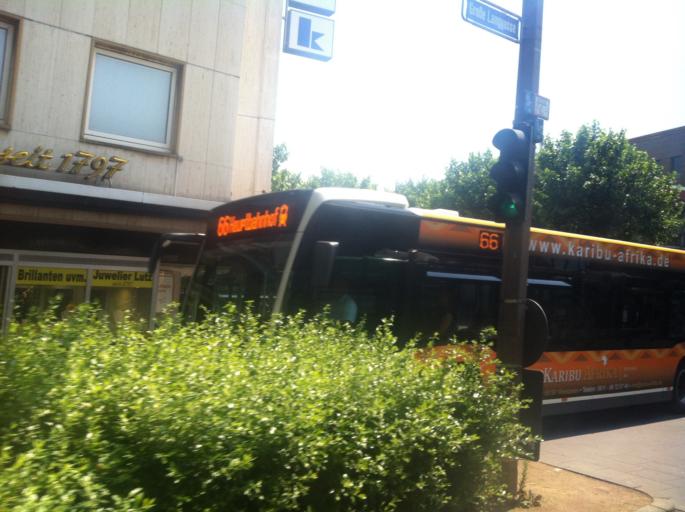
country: DE
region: Rheinland-Pfalz
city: Mainz
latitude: 49.9985
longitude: 8.2693
